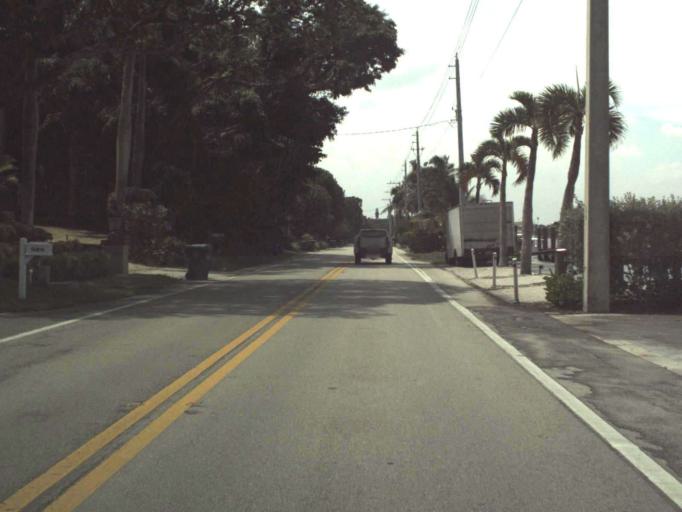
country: US
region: Florida
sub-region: Broward County
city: Lighthouse Point
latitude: 26.2718
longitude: -80.0805
